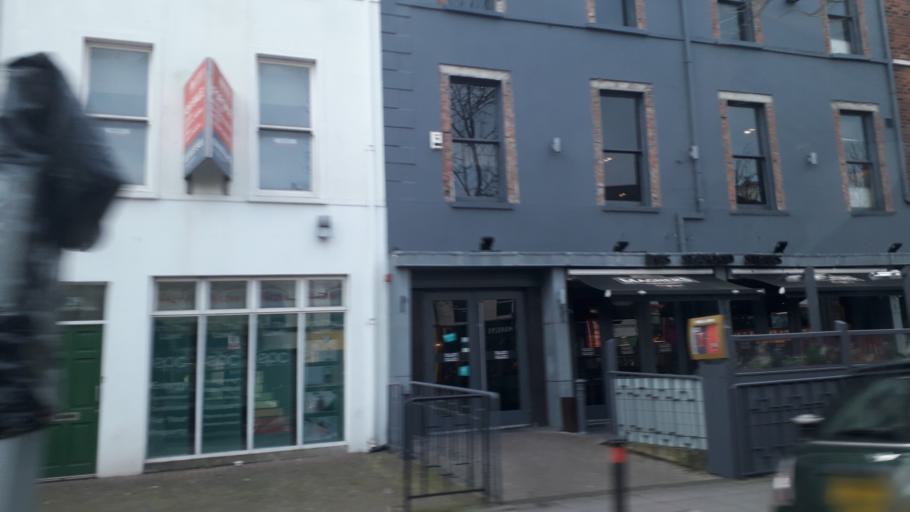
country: GB
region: Northern Ireland
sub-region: City of Belfast
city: Belfast
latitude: 54.5866
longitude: -5.9360
